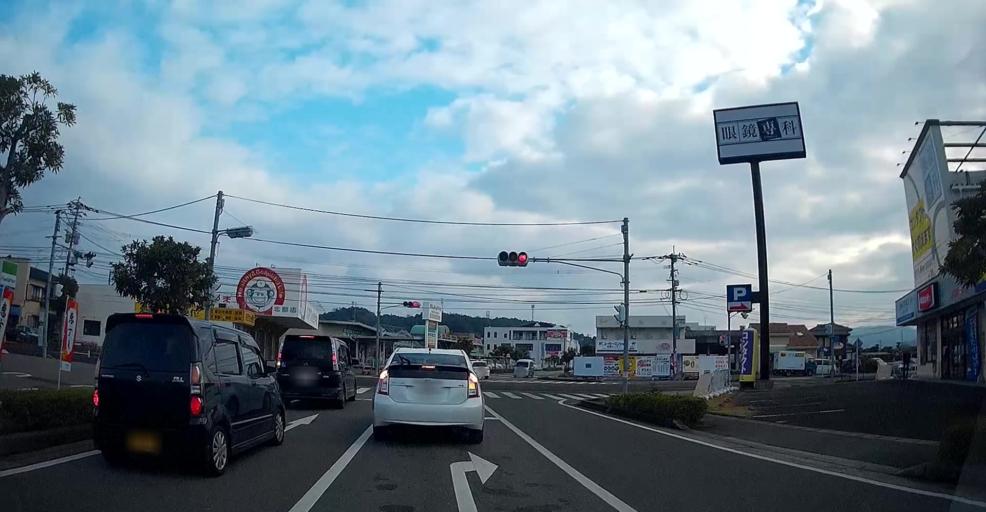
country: JP
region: Kumamoto
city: Hondo
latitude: 32.4647
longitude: 130.1893
